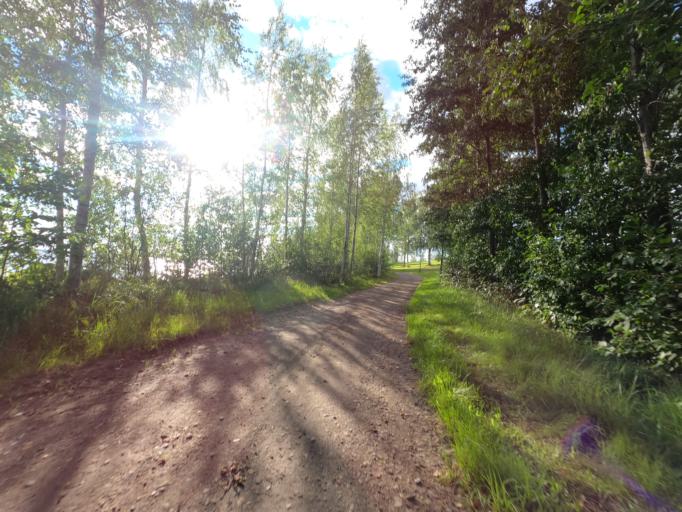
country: FI
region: North Karelia
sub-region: Joensuu
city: Joensuu
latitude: 62.5941
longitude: 29.7340
